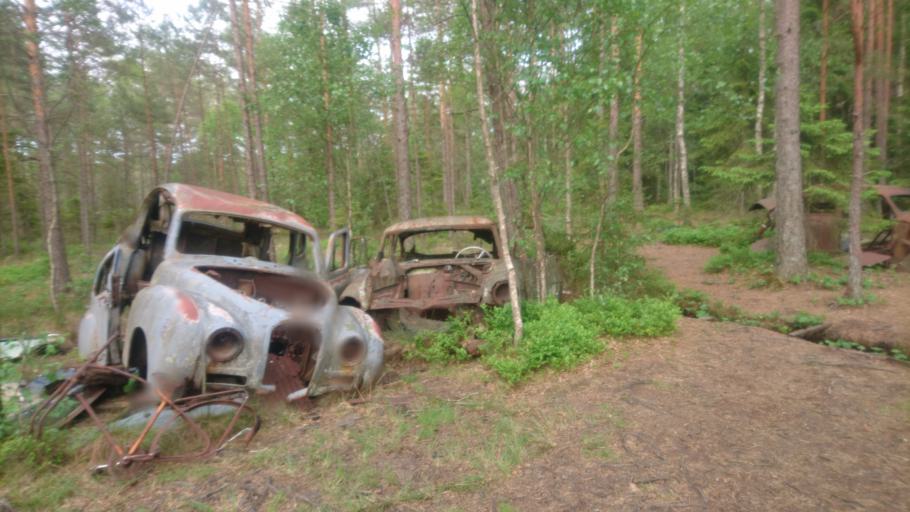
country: SE
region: Blekinge
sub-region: Olofstroms Kommun
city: Olofstroem
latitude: 56.4669
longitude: 14.6497
